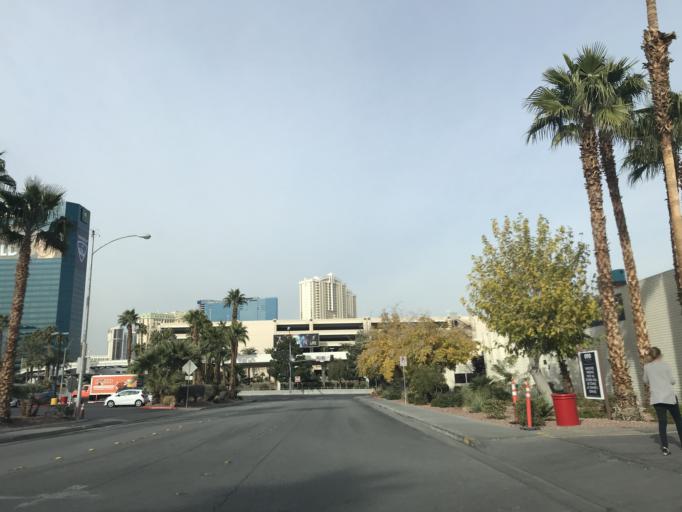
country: US
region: Nevada
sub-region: Clark County
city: Paradise
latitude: 36.0999
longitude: -115.1666
